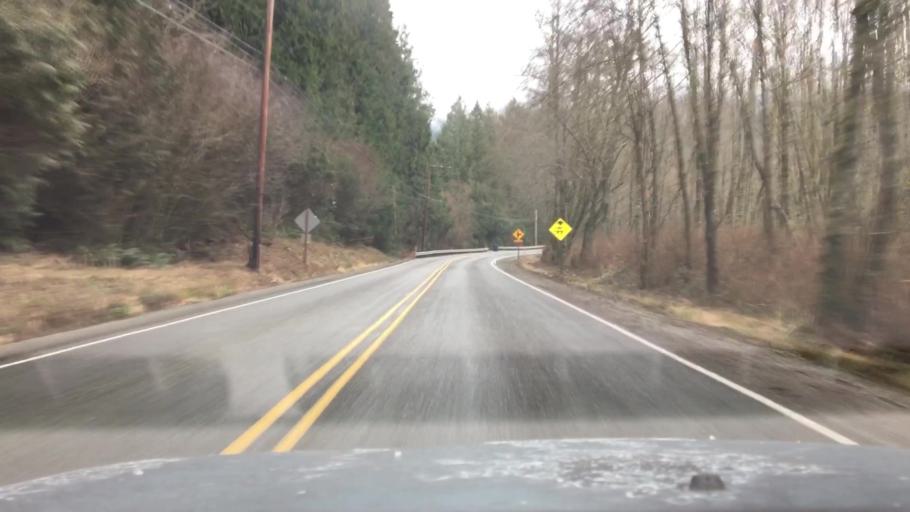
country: US
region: Washington
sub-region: Whatcom County
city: Sudden Valley
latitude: 48.6404
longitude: -122.3169
